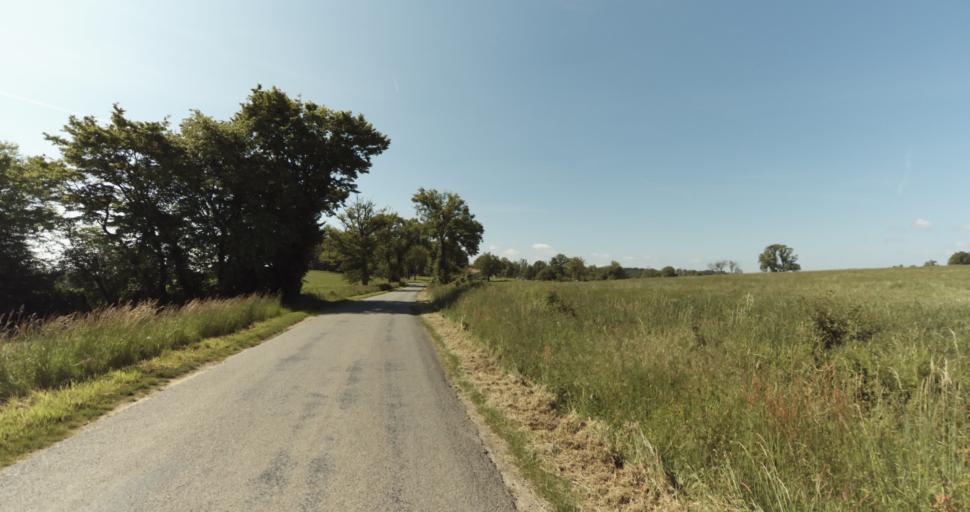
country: FR
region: Limousin
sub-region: Departement de la Haute-Vienne
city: Le Vigen
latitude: 45.7178
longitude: 1.2886
